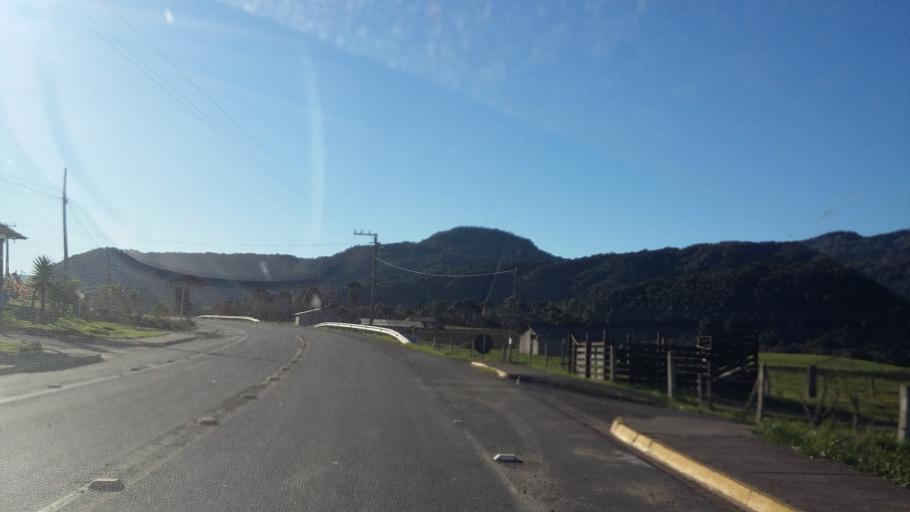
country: BR
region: Santa Catarina
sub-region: Lauro Muller
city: Lauro Muller
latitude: -28.0225
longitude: -49.5002
